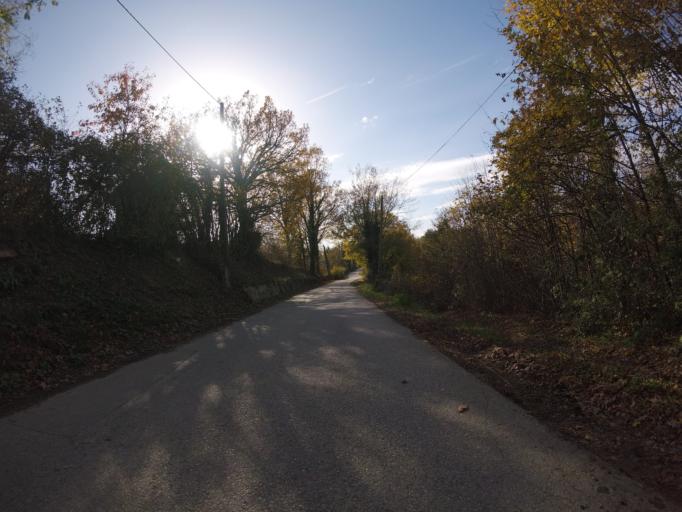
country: HR
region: Zagrebacka
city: Lukavec
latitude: 45.6130
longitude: 16.0063
